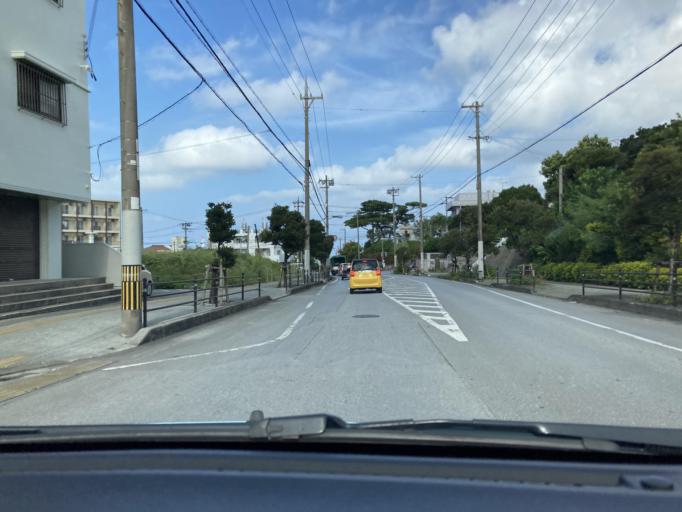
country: JP
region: Okinawa
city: Ginowan
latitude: 26.2629
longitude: 127.7496
